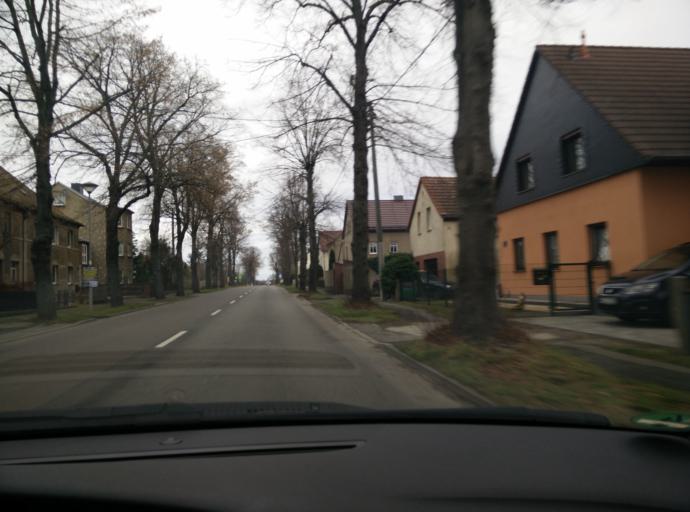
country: DE
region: Saxony
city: Frohburg
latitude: 51.0850
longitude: 12.5310
